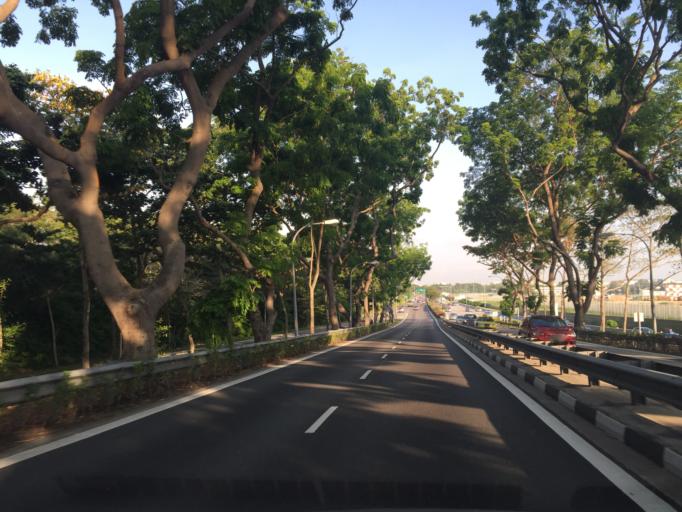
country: SG
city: Singapore
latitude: 1.3375
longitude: 103.9786
